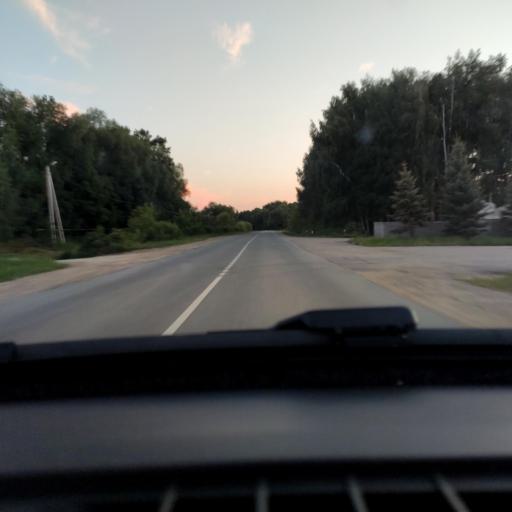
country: RU
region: Lipetsk
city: Zadonsk
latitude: 52.3000
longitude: 38.8561
